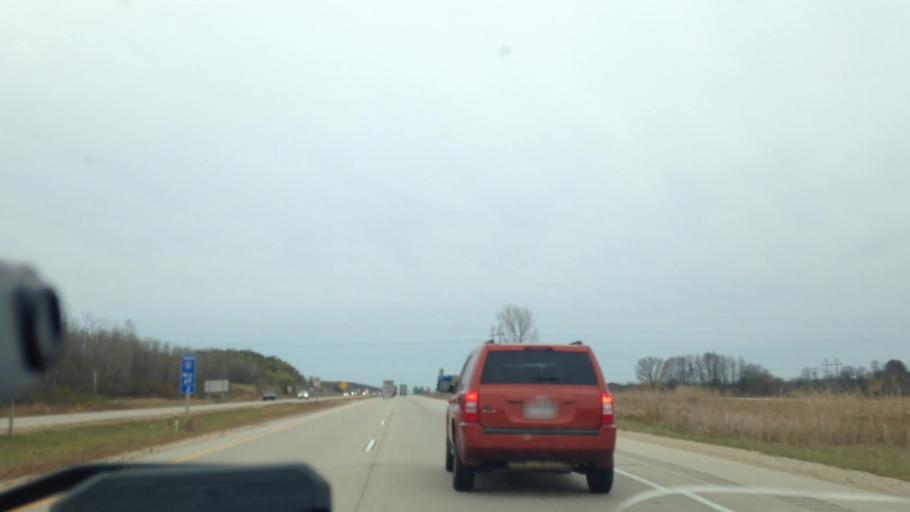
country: US
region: Wisconsin
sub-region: Washington County
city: Slinger
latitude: 43.3809
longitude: -88.3058
